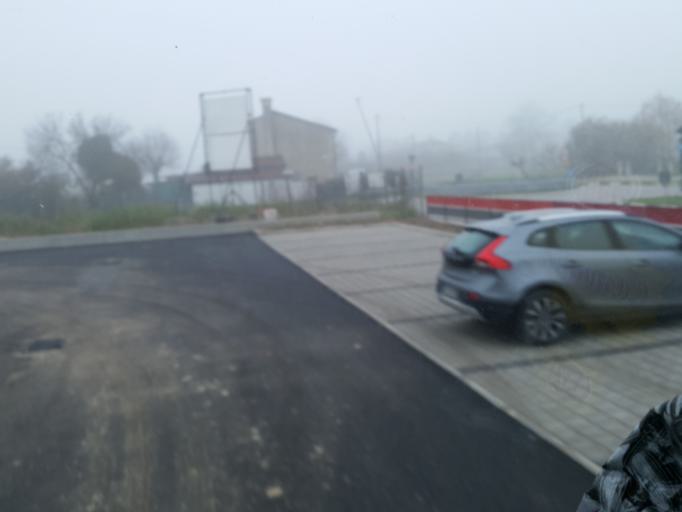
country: IT
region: Veneto
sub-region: Provincia di Padova
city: Borgoricco-San Michele delle Badesse-Sant'Eufemia
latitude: 45.5400
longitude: 11.9502
